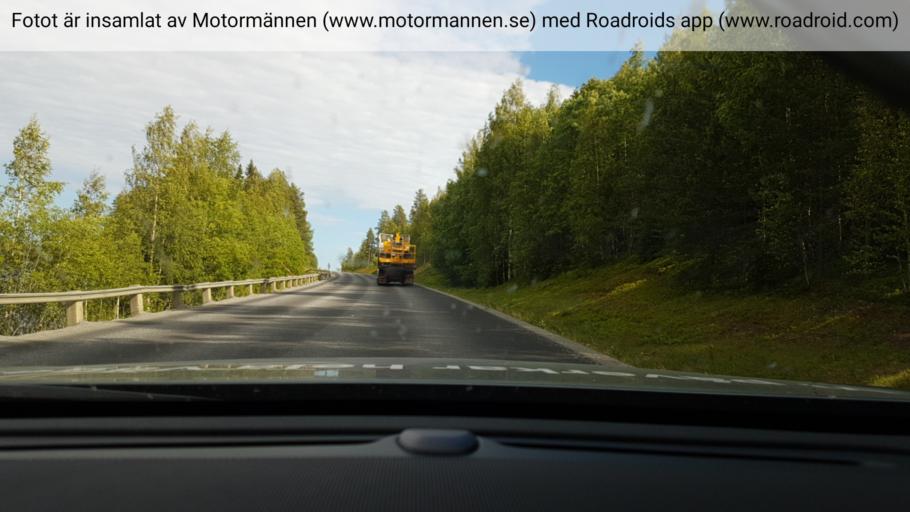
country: SE
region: Vaesterbotten
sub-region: Lycksele Kommun
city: Soderfors
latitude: 64.8415
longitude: 17.9764
